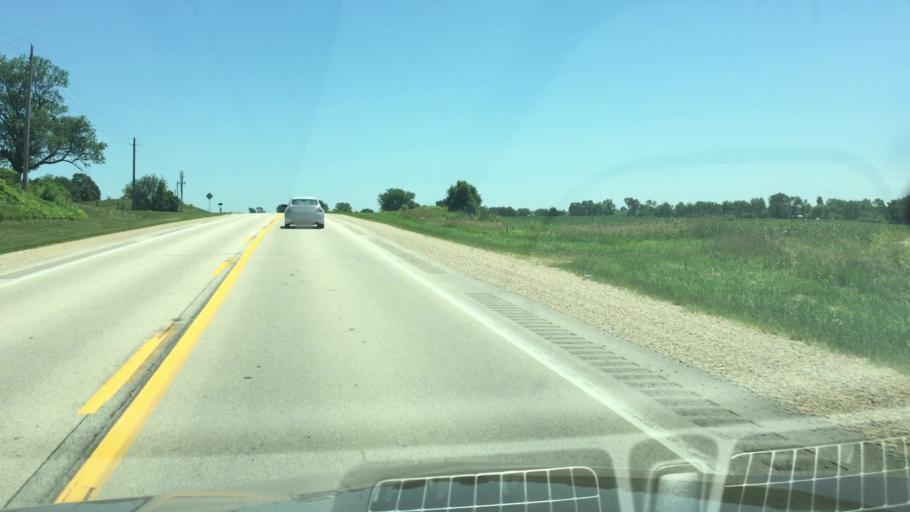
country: US
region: Iowa
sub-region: Jackson County
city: Maquoketa
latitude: 42.0713
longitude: -90.7967
